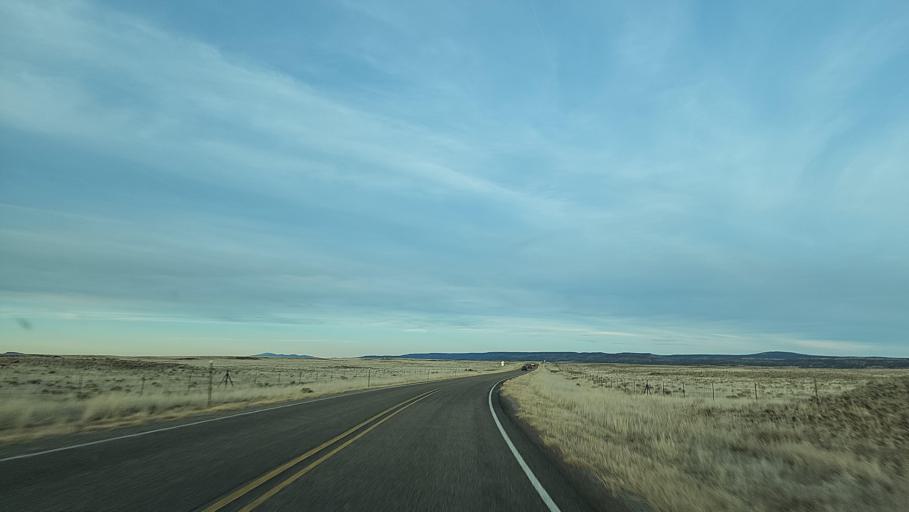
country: US
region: New Mexico
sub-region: Cibola County
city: Grants
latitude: 34.6821
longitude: -108.0743
